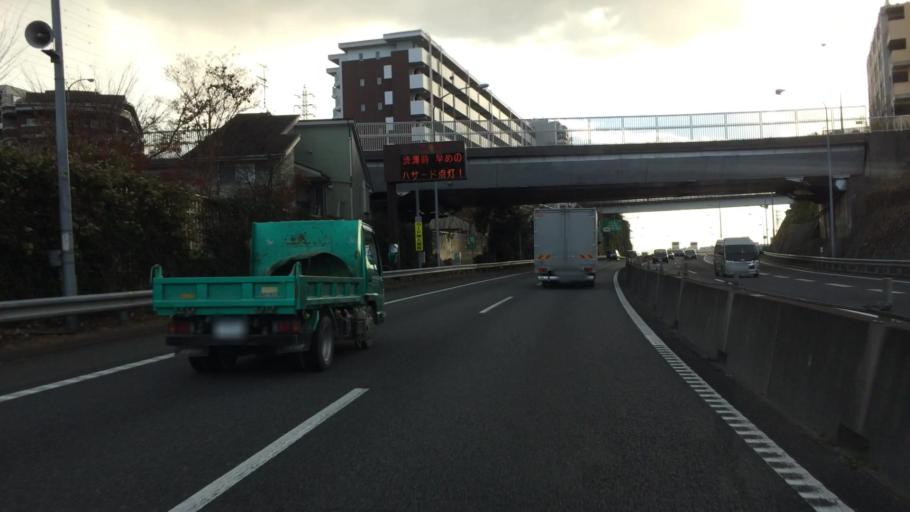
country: JP
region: Kanagawa
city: Yokohama
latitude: 35.4344
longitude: 139.5544
